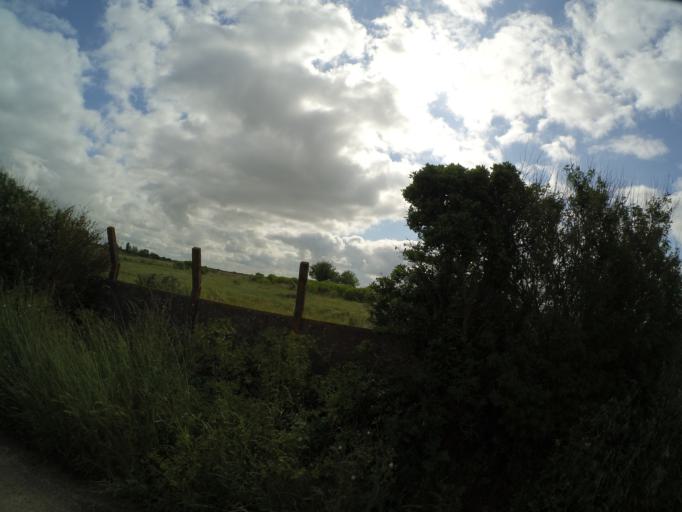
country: FR
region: Poitou-Charentes
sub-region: Departement de la Charente-Maritime
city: Angoulins
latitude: 46.1115
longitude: -1.1210
